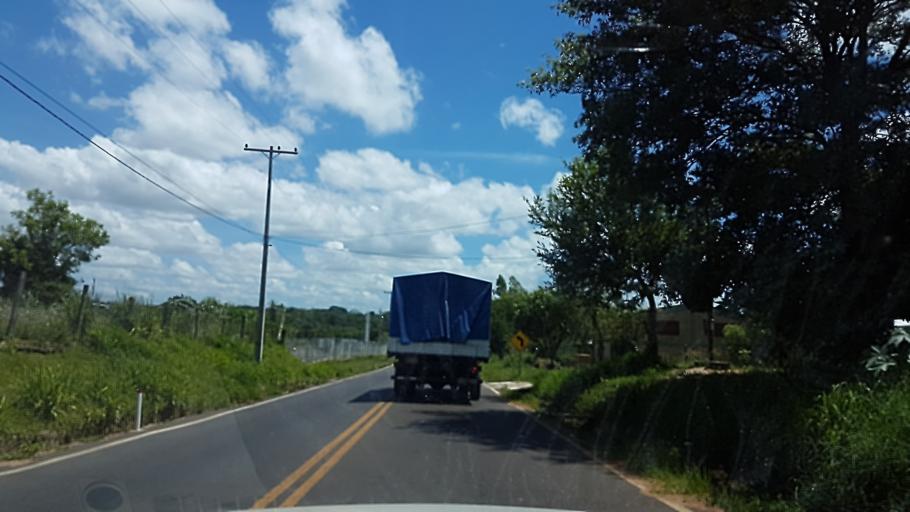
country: PY
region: Central
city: Capiata
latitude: -25.3175
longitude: -57.4533
